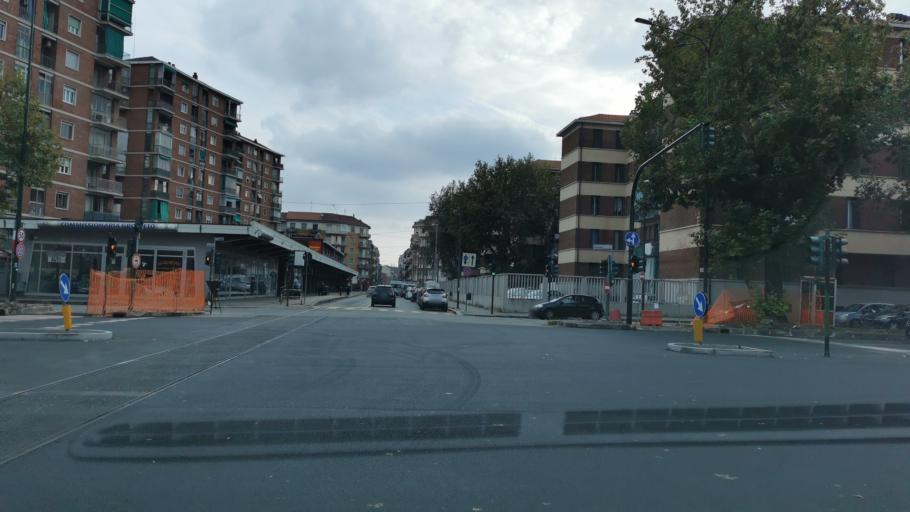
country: IT
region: Piedmont
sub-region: Provincia di Torino
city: Turin
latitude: 45.1044
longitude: 7.6814
